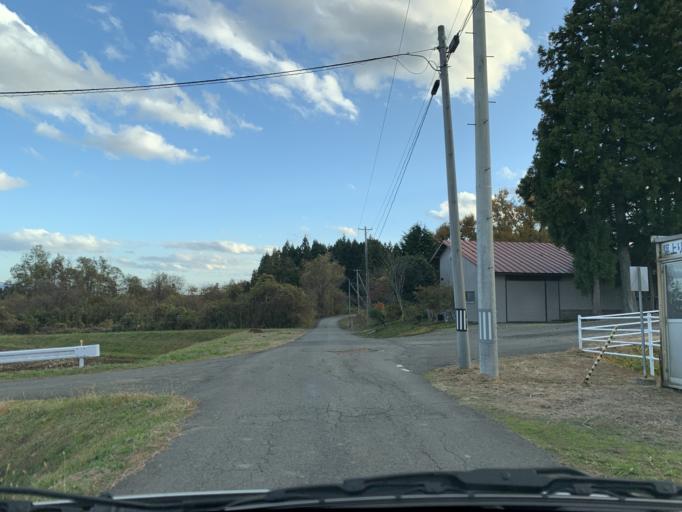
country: JP
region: Iwate
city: Mizusawa
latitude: 39.1096
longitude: 141.0391
